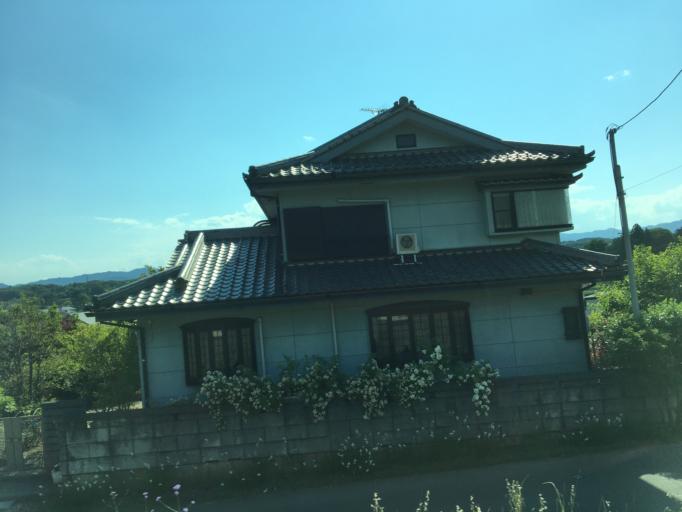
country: JP
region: Saitama
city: Morohongo
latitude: 35.9730
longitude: 139.3393
